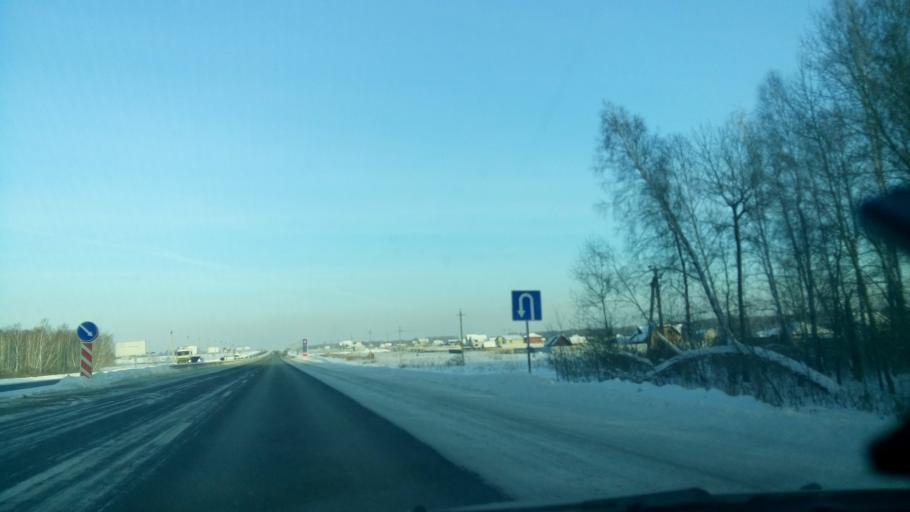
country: RU
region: Chelyabinsk
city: Dolgoderevenskoye
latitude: 55.3705
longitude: 61.3334
